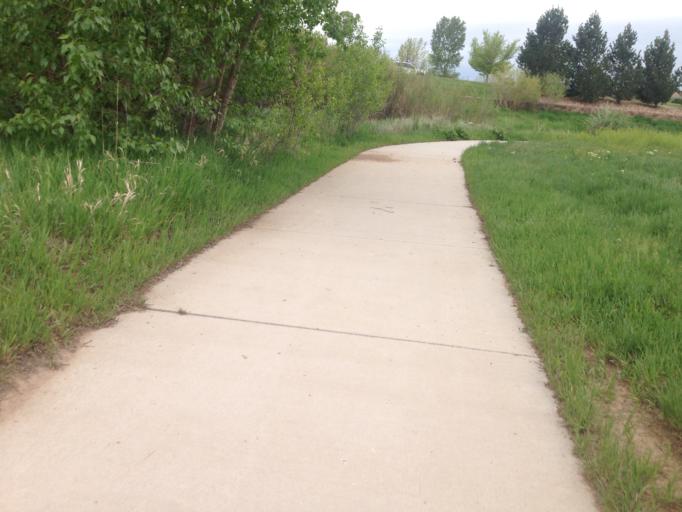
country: US
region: Colorado
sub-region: Boulder County
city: Longmont
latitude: 40.1531
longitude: -105.0905
